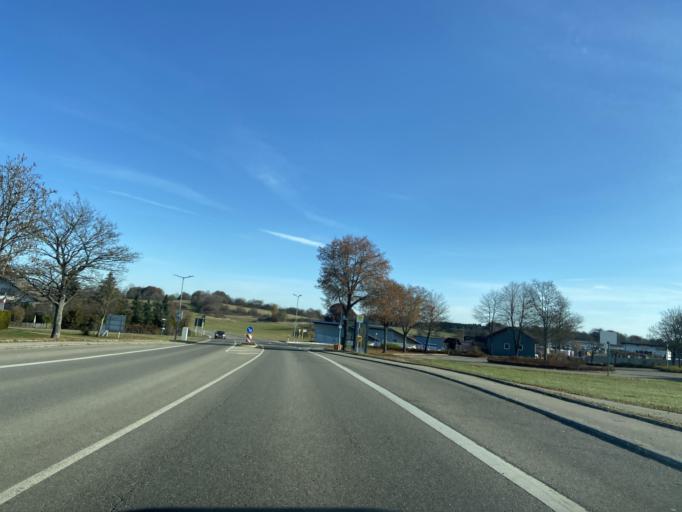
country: DE
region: Baden-Wuerttemberg
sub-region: Tuebingen Region
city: Schwenningen
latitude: 48.1078
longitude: 9.0024
